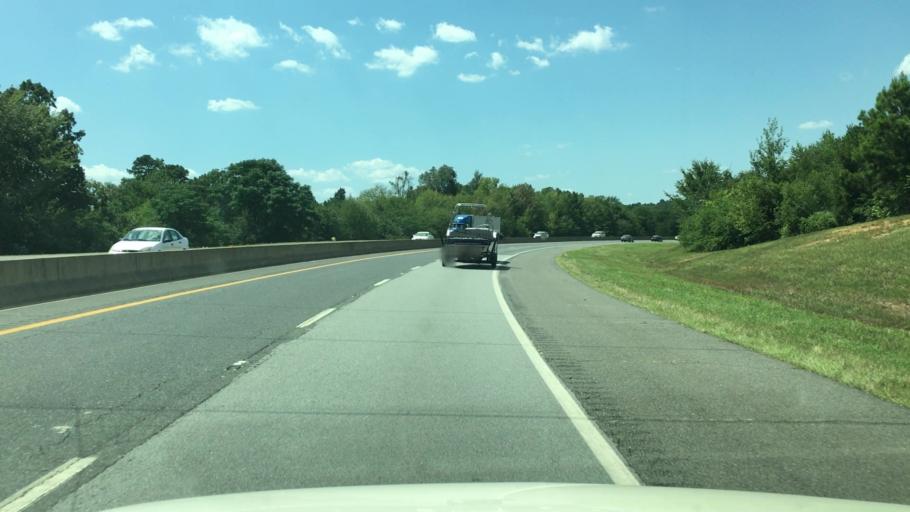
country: US
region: Arkansas
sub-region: Garland County
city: Rockwell
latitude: 34.4714
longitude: -93.1125
